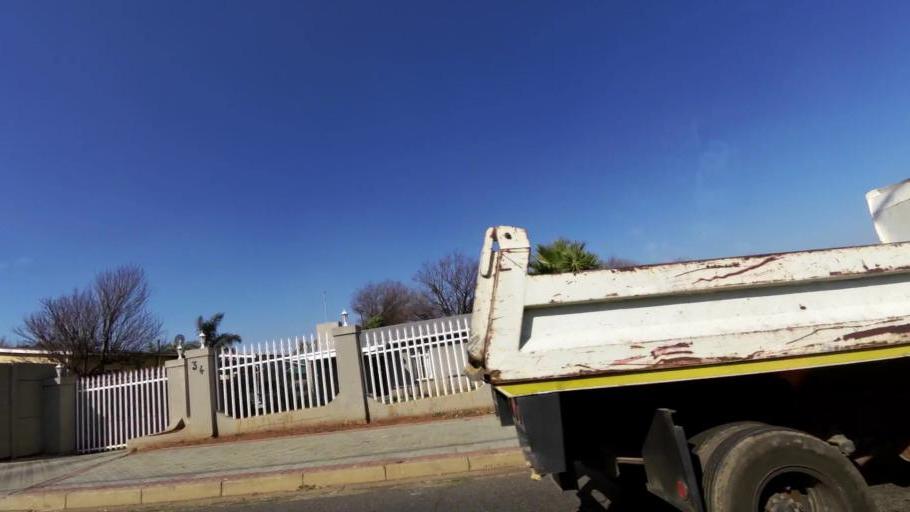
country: ZA
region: Gauteng
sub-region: City of Johannesburg Metropolitan Municipality
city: Johannesburg
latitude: -26.1781
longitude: 27.9823
